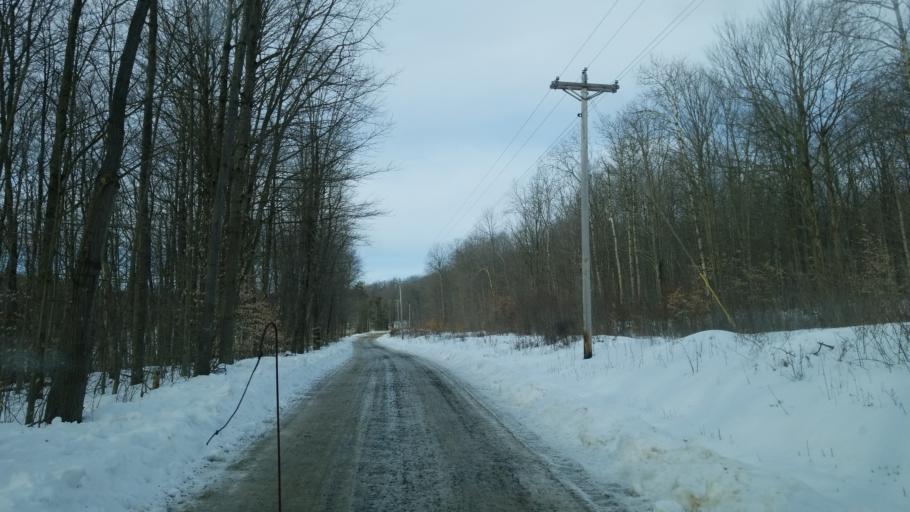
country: US
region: Pennsylvania
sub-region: Tioga County
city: Westfield
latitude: 41.9598
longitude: -77.7223
